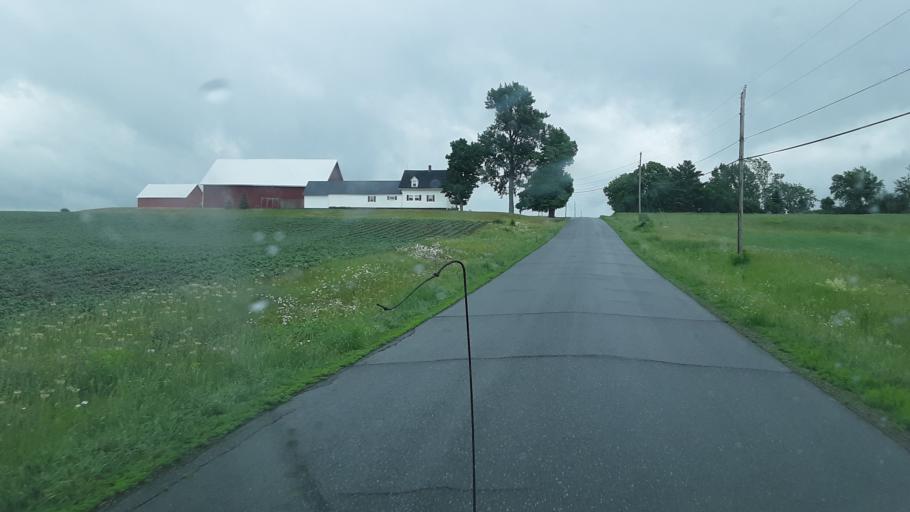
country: US
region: Maine
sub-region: Aroostook County
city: Presque Isle
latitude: 46.6817
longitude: -68.1910
